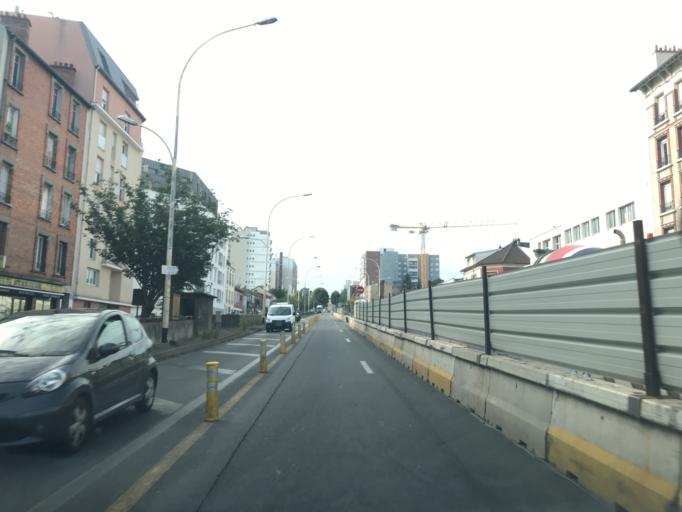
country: FR
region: Ile-de-France
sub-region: Departement du Val-de-Marne
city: Villejuif
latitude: 48.8034
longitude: 2.3644
